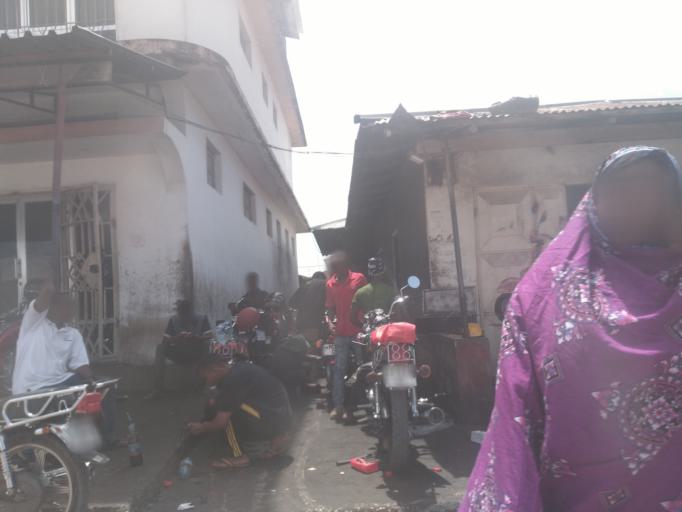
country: TZ
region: Zanzibar Urban/West
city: Zanzibar
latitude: -6.1623
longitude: 39.2085
